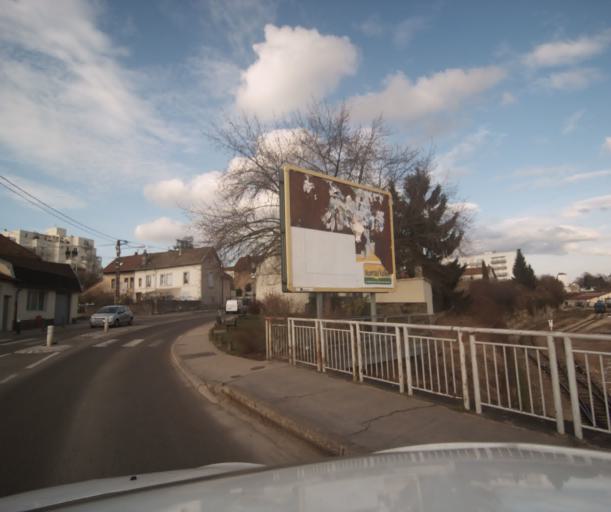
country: FR
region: Franche-Comte
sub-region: Departement du Doubs
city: Besancon
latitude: 47.2516
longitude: 6.0302
